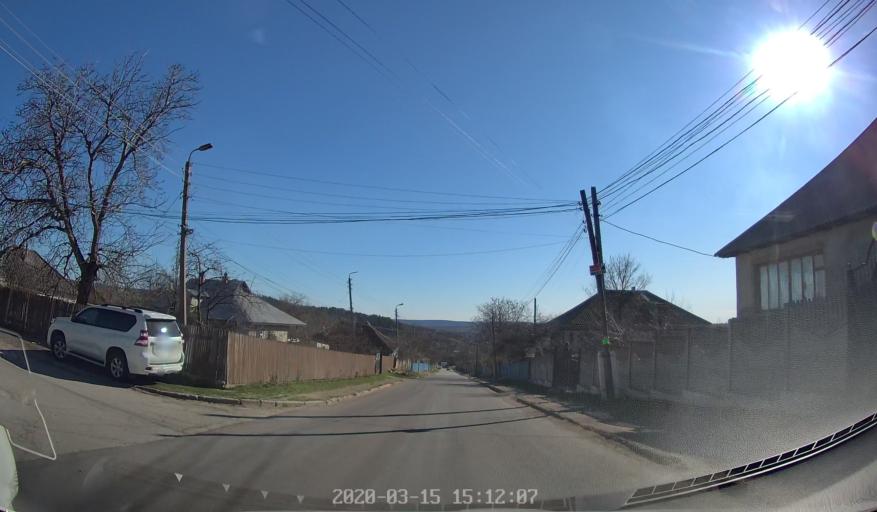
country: MD
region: Orhei
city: Orhei
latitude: 47.2579
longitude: 28.7743
